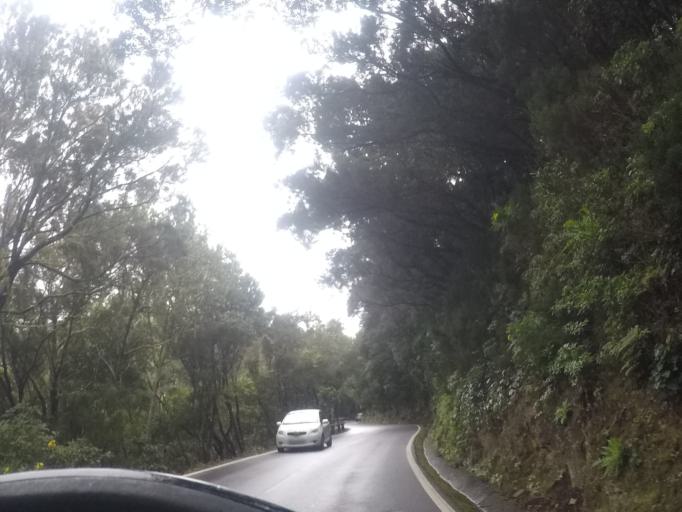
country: ES
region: Canary Islands
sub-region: Provincia de Santa Cruz de Tenerife
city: Tegueste
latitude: 28.5259
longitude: -16.2839
